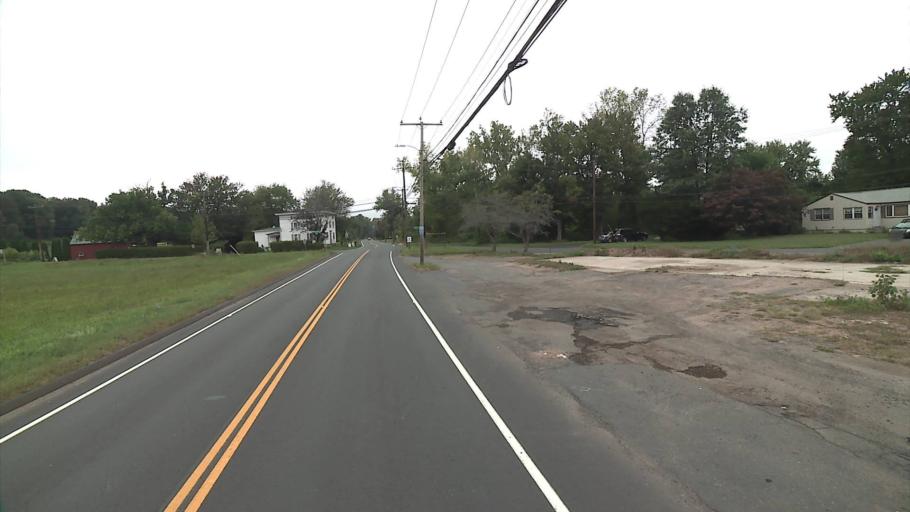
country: US
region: Connecticut
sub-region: Hartford County
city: Windsor
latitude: 41.8617
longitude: -72.6534
